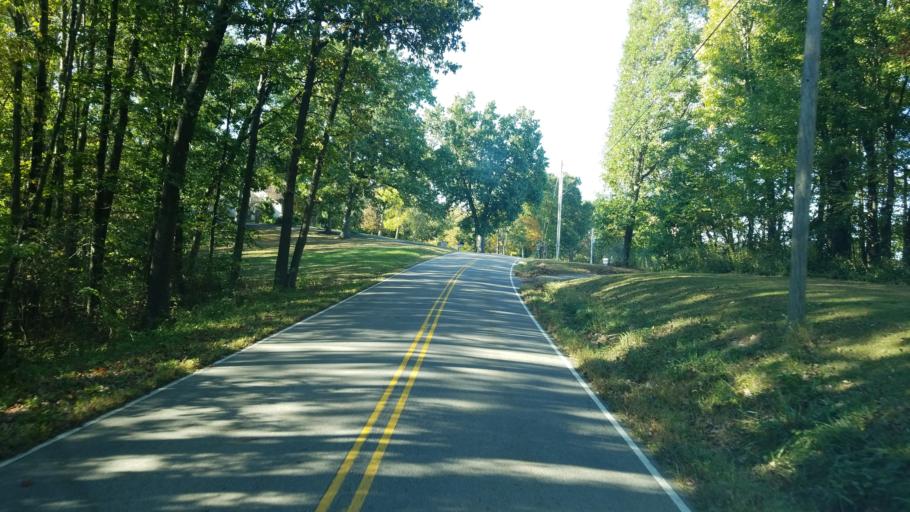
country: US
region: Ohio
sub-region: Licking County
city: Utica
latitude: 40.1659
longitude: -82.3784
